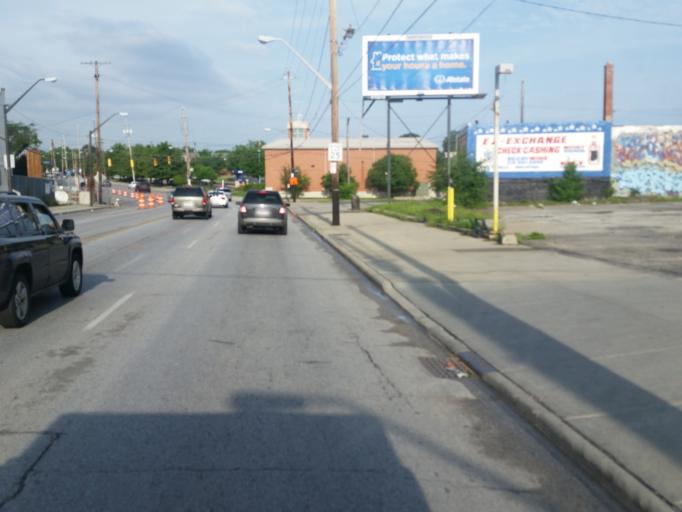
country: US
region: Ohio
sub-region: Cuyahoga County
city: Bratenahl
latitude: 41.5401
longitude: -81.6120
